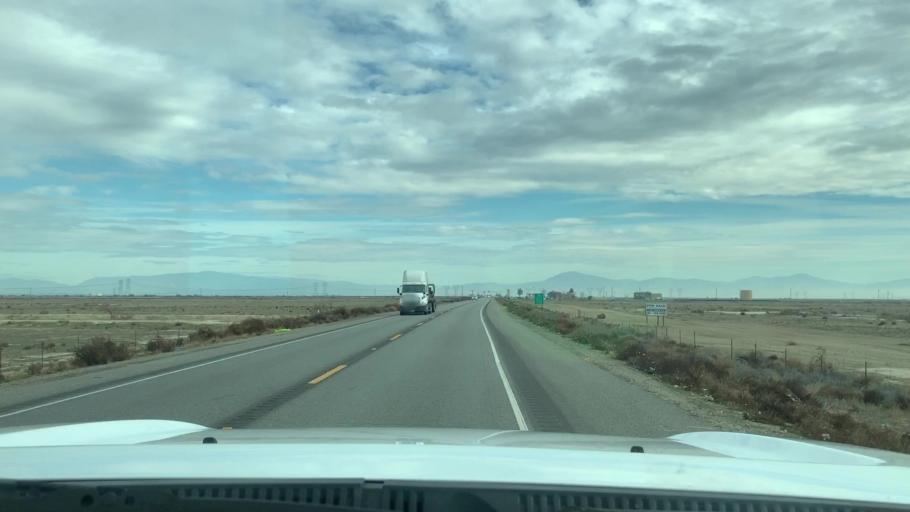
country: US
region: California
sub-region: Kern County
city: Rosedale
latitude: 35.2675
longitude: -119.2626
